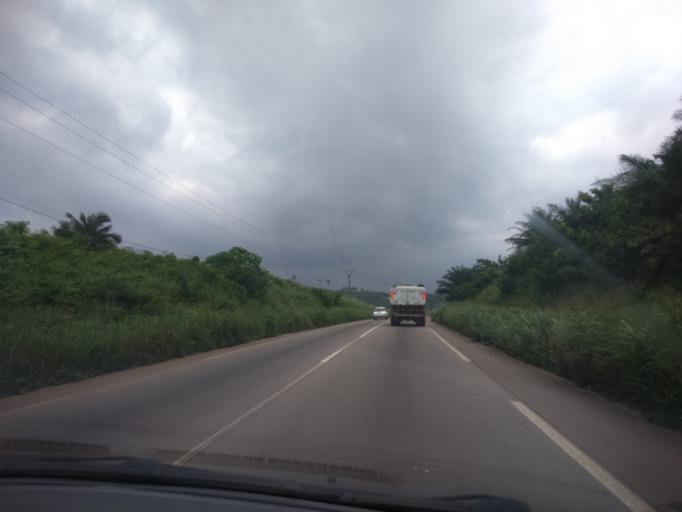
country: CI
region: Lagunes
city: Anyama
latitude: 5.5009
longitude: -4.0654
